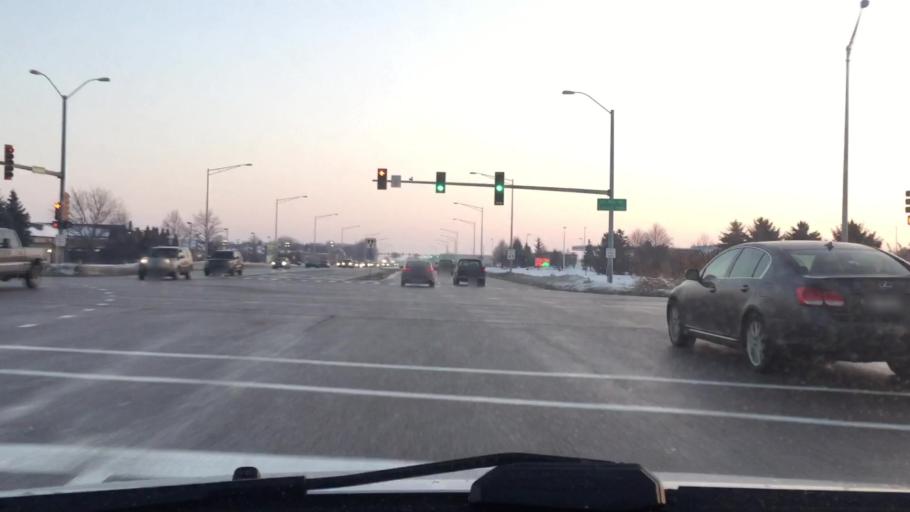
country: US
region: Illinois
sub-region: Kane County
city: Saint Charles
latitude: 41.9021
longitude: -88.3400
